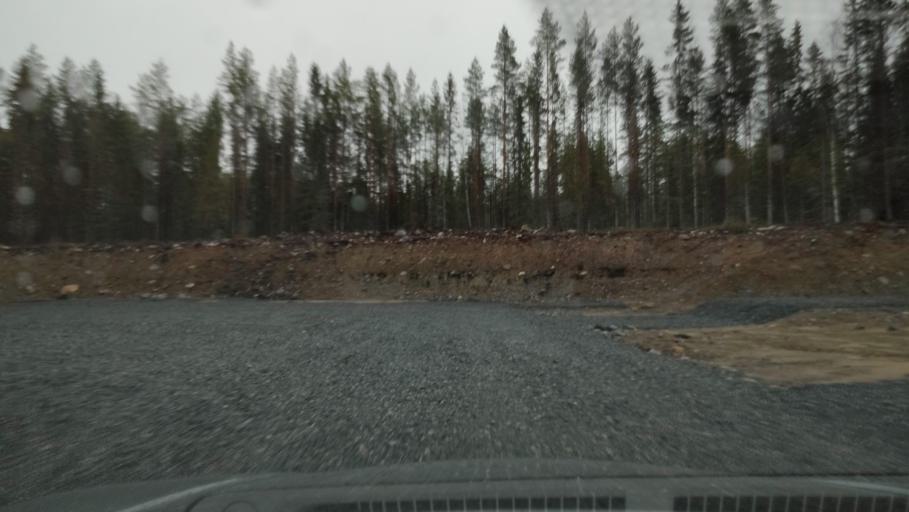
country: FI
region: Southern Ostrobothnia
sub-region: Suupohja
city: Karijoki
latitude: 62.1491
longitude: 21.6359
